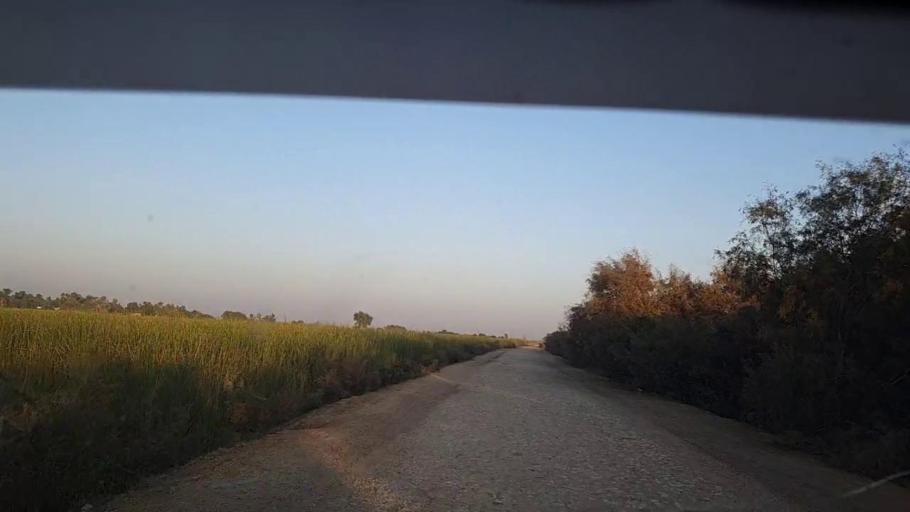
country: PK
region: Sindh
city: Ratodero
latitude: 27.8984
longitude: 68.2477
